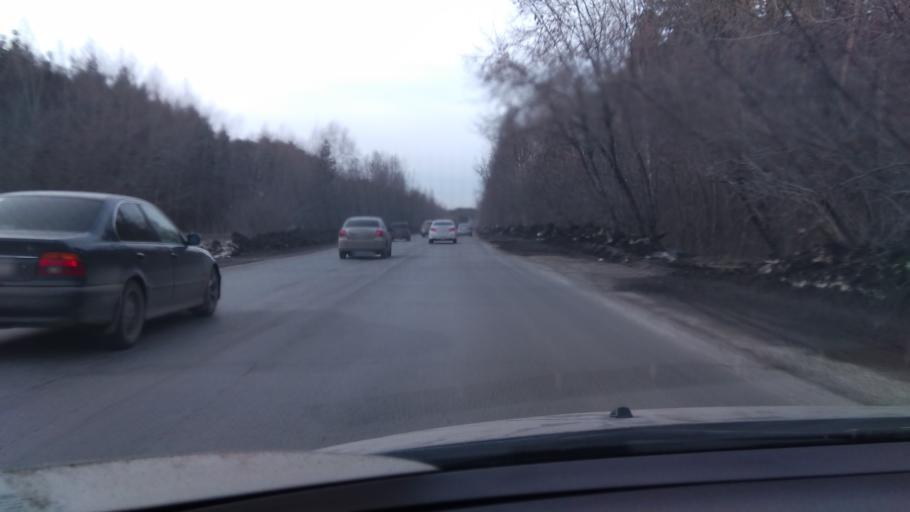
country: RU
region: Sverdlovsk
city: Shirokaya Rechka
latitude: 56.8076
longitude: 60.5307
